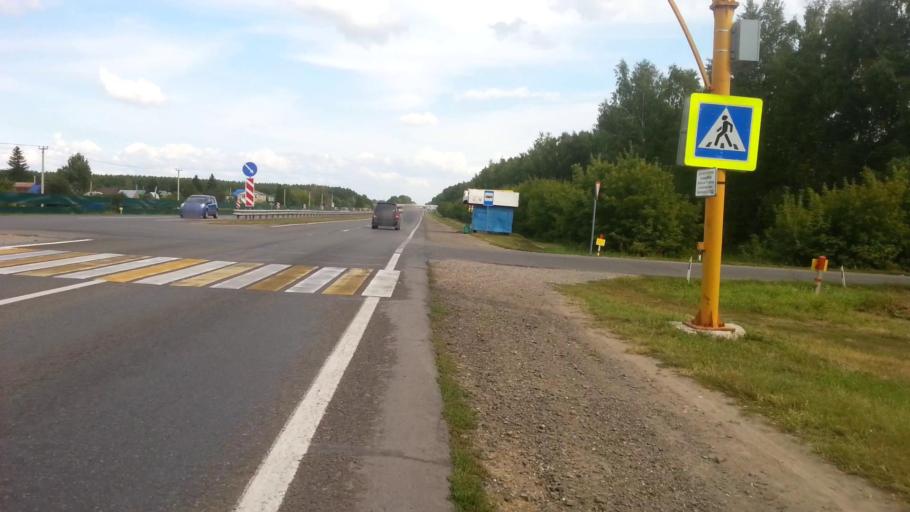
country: RU
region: Altai Krai
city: Vlasikha
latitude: 53.3544
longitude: 83.5404
